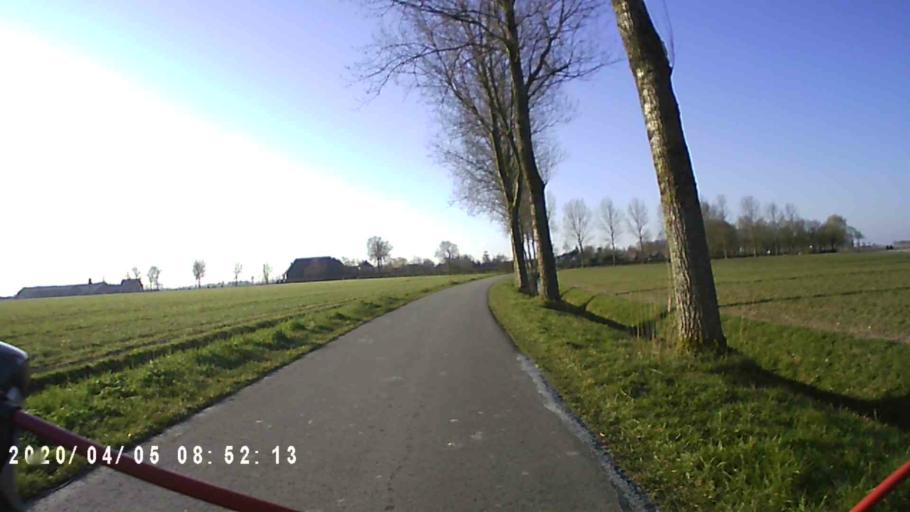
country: NL
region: Groningen
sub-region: Gemeente Zuidhorn
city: Aduard
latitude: 53.3111
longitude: 6.4653
